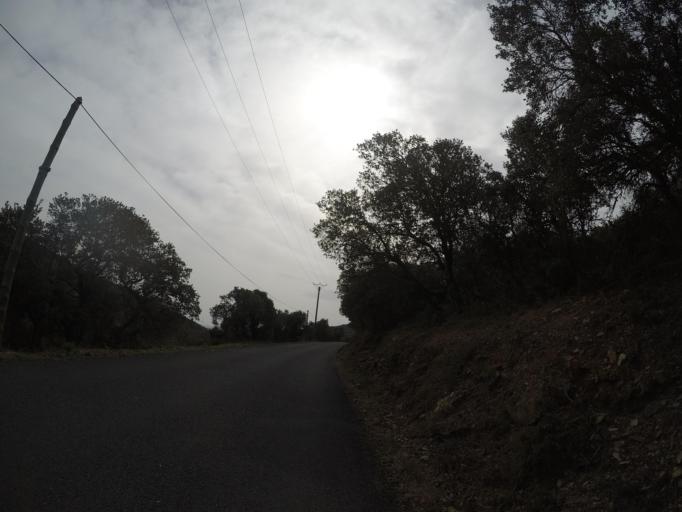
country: FR
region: Languedoc-Roussillon
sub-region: Departement des Pyrenees-Orientales
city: Corneilla-la-Riviere
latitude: 42.7339
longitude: 2.7330
